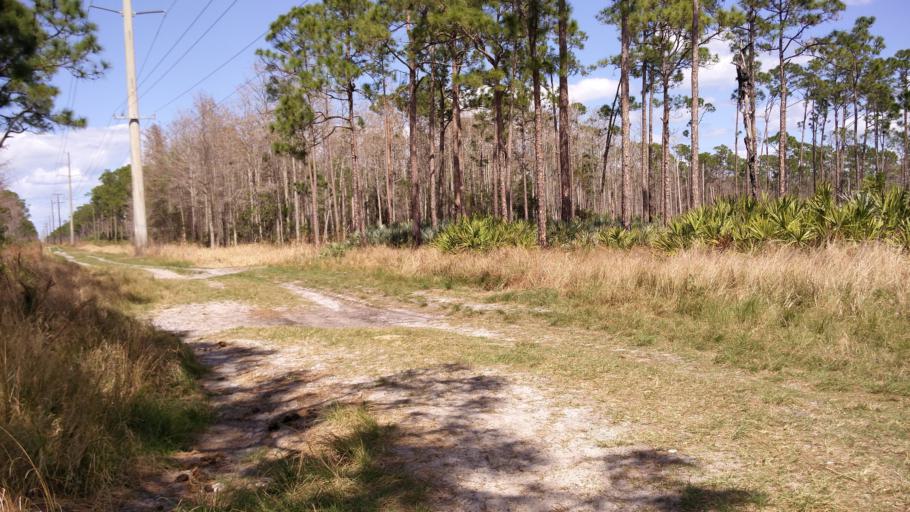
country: US
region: Florida
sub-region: Palm Beach County
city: Tequesta
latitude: 27.0069
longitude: -80.1414
